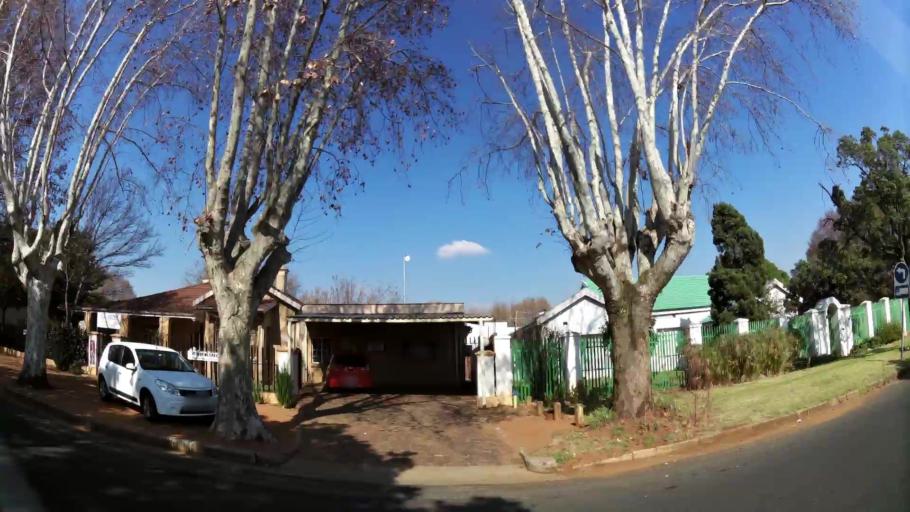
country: ZA
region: Gauteng
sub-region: Ekurhuleni Metropolitan Municipality
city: Benoni
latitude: -26.1972
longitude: 28.3004
